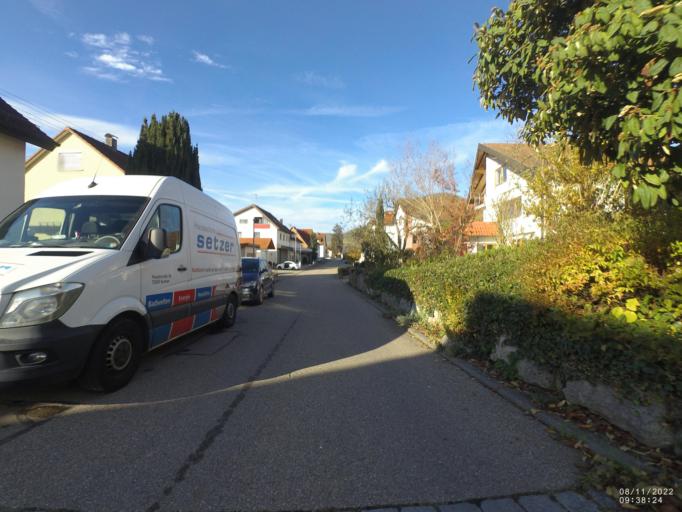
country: DE
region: Baden-Wuerttemberg
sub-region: Regierungsbezirk Stuttgart
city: Bad Uberkingen
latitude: 48.6076
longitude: 9.7677
